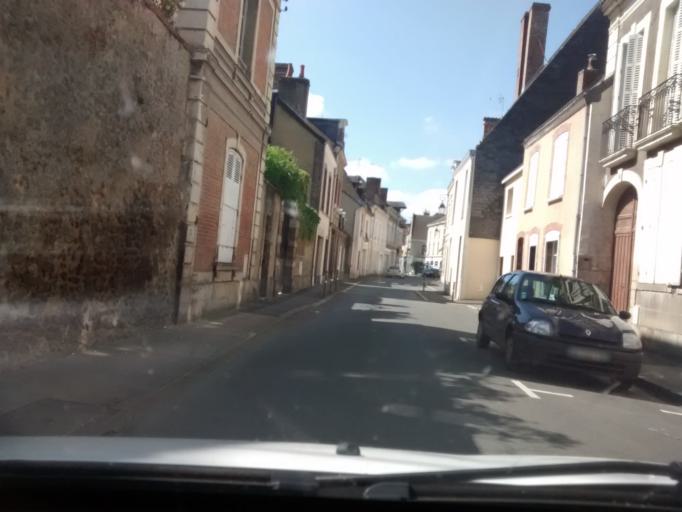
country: FR
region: Pays de la Loire
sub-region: Departement de la Sarthe
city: Saint-Calais
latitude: 47.9228
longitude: 0.7458
